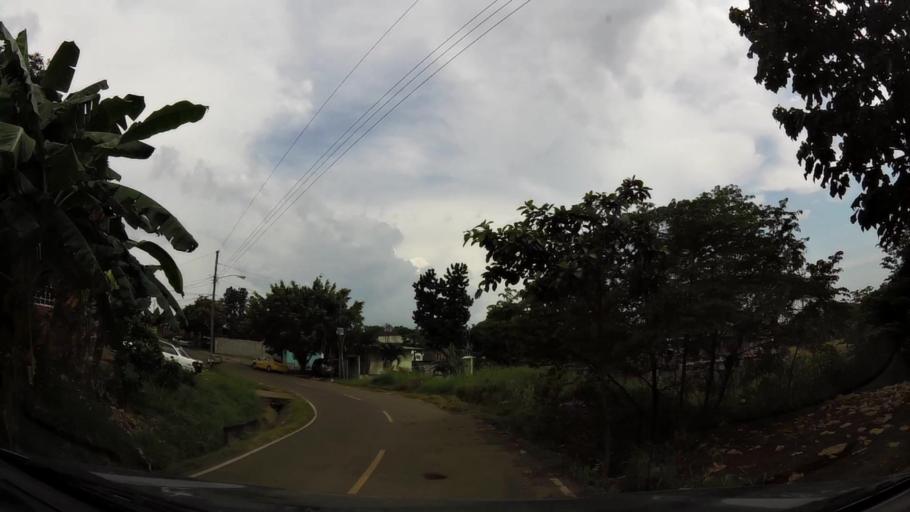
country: PA
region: Panama
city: Tocumen
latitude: 9.1113
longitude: -79.3779
